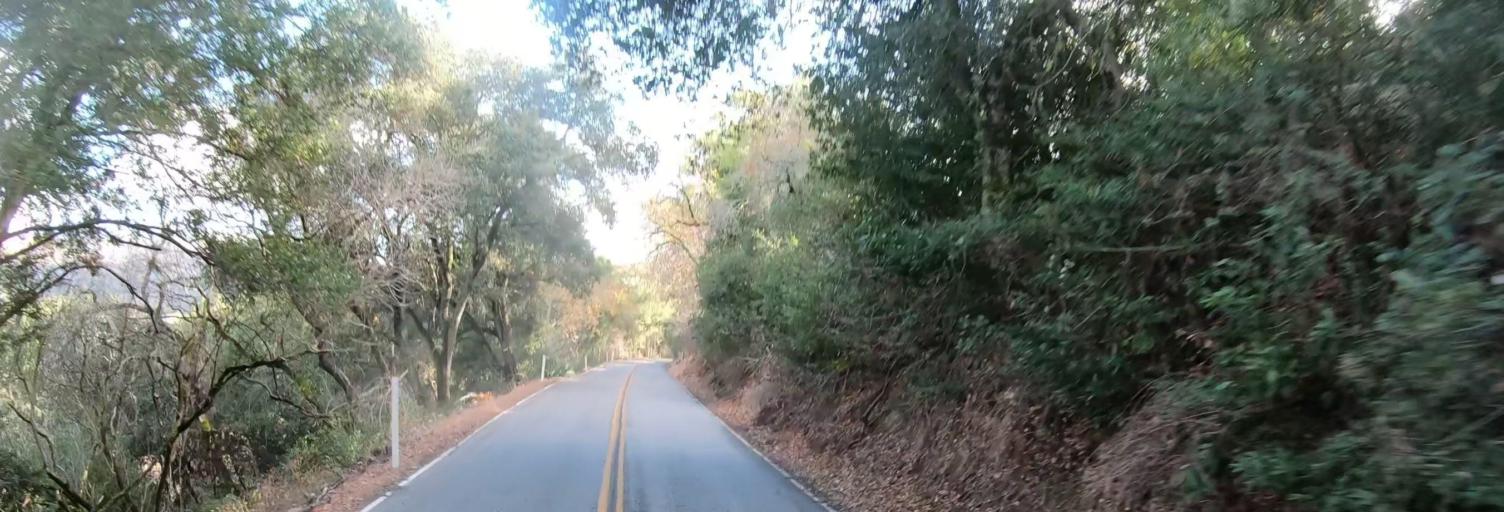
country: US
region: California
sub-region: Santa Clara County
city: East Foothills
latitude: 37.3516
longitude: -121.7337
